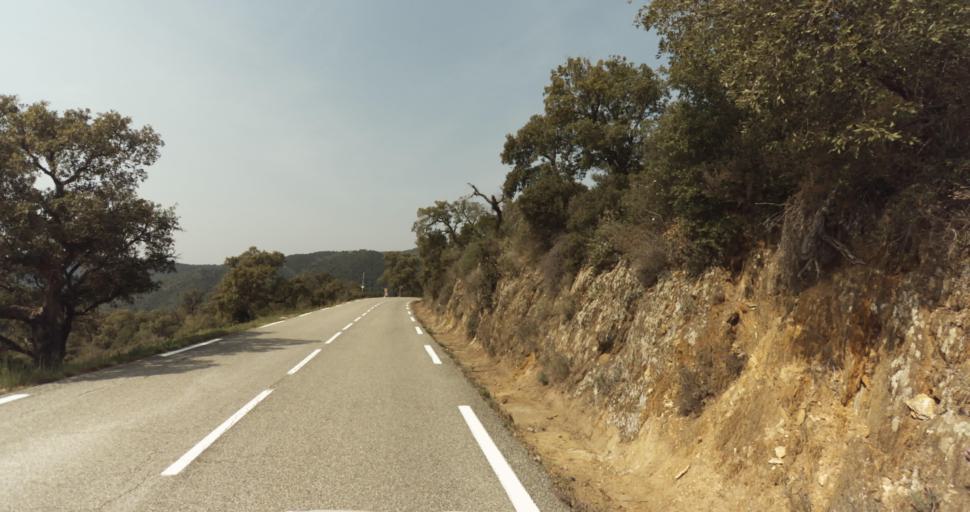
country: FR
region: Provence-Alpes-Cote d'Azur
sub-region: Departement du Var
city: Bormes-les-Mimosas
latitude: 43.1650
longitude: 6.3320
